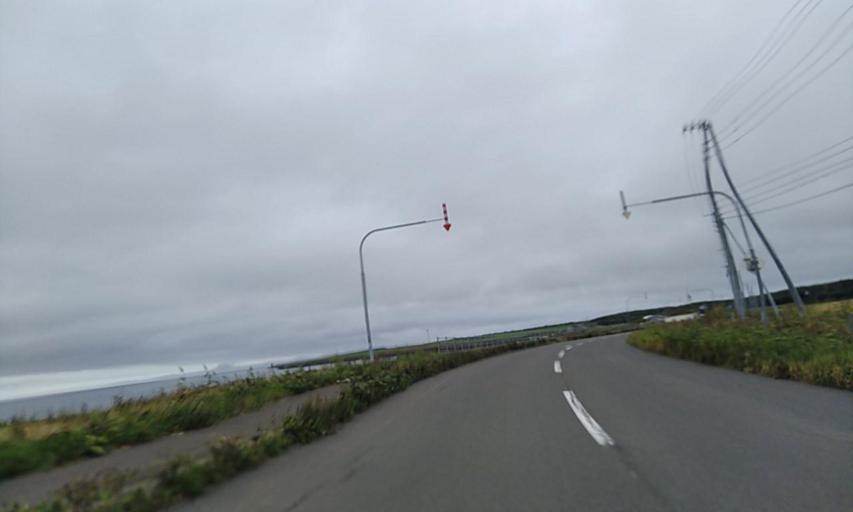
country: JP
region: Hokkaido
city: Nemuro
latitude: 43.3688
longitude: 145.6289
